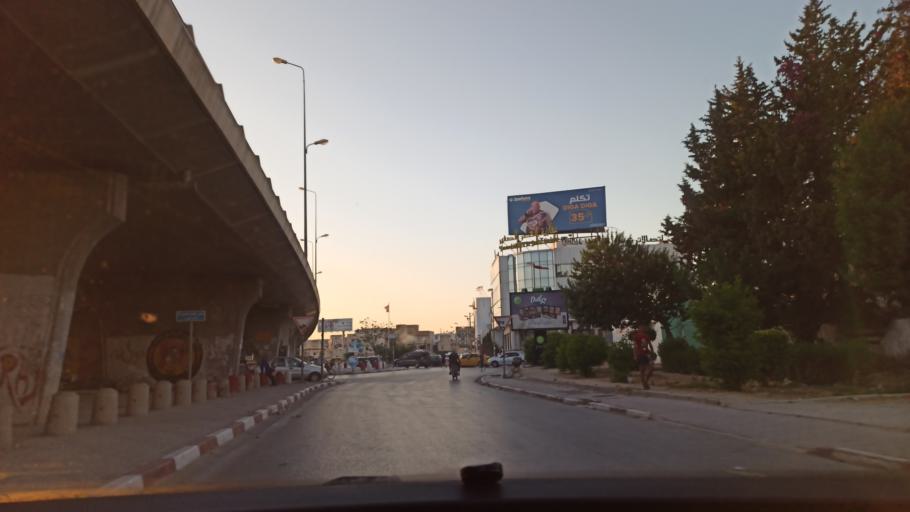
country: TN
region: Ariana
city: Ariana
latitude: 36.8641
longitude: 10.2009
